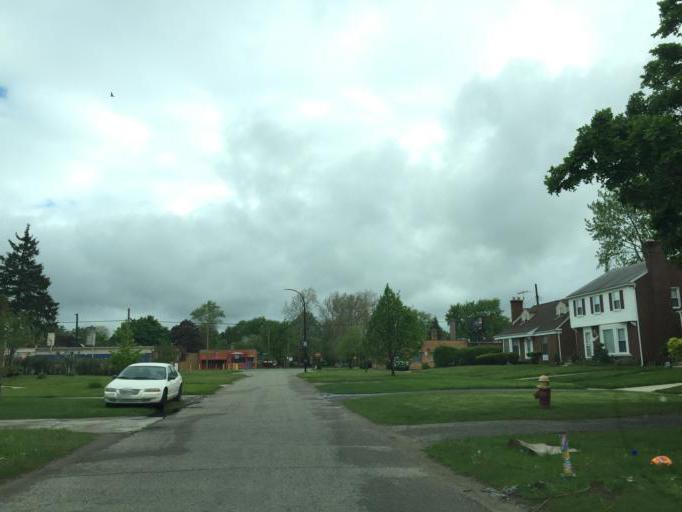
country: US
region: Michigan
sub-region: Oakland County
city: Southfield
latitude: 42.4143
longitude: -83.2228
